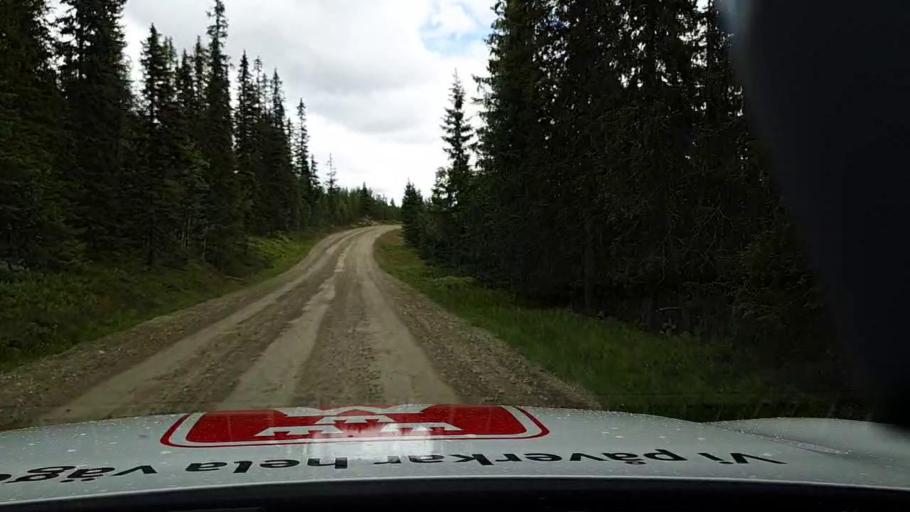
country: SE
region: Jaemtland
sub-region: Are Kommun
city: Jarpen
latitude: 62.6004
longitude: 13.2341
